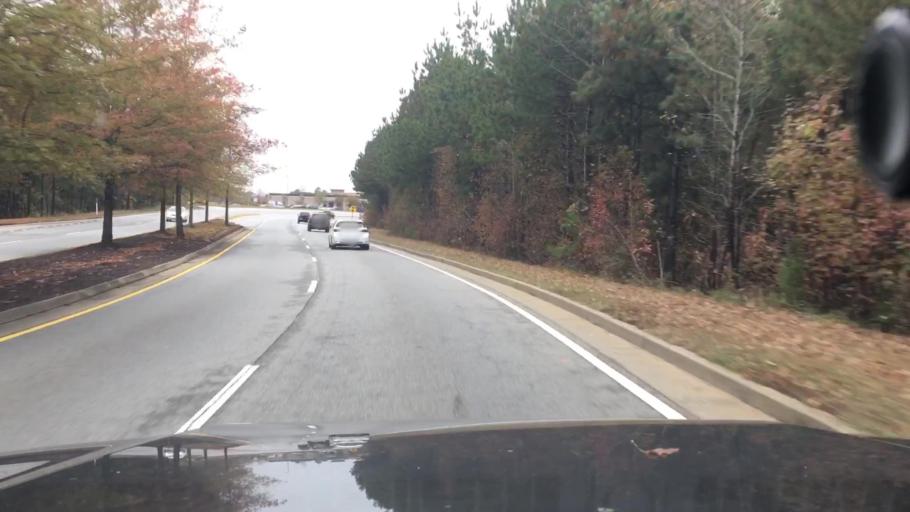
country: US
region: Georgia
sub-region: Coweta County
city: East Newnan
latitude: 33.3809
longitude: -84.7611
